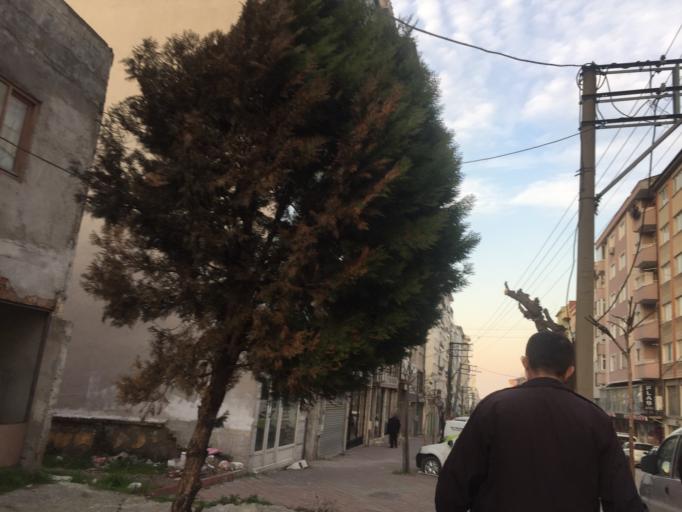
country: TR
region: Bursa
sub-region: Osmangazi
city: Bursa
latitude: 40.1855
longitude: 29.0761
